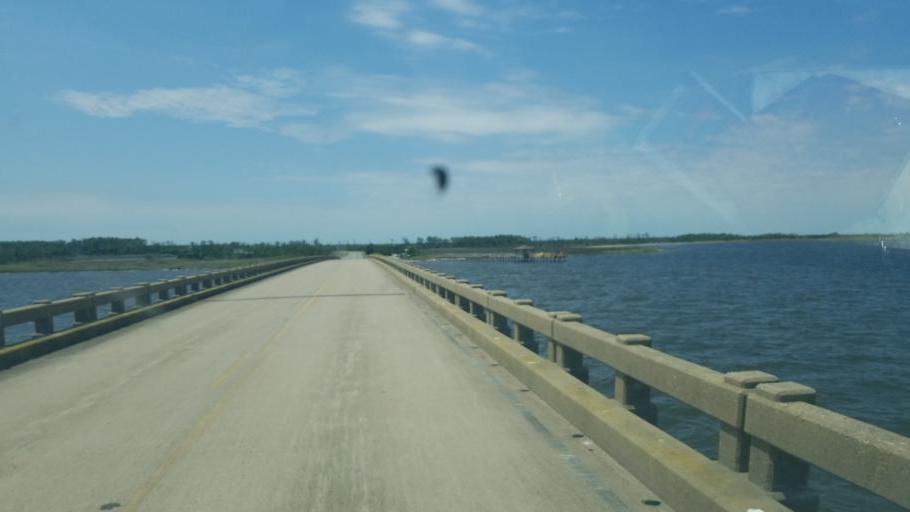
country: US
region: North Carolina
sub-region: Dare County
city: Manteo
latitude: 35.9130
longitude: -75.7655
